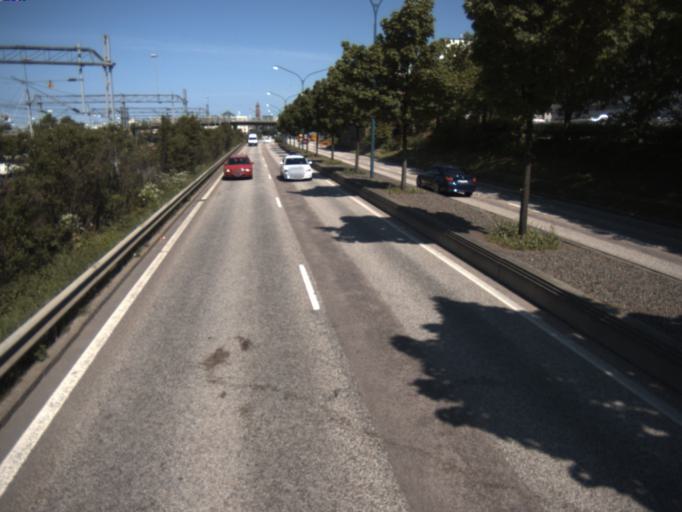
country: SE
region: Skane
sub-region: Helsingborg
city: Helsingborg
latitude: 56.0388
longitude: 12.7000
